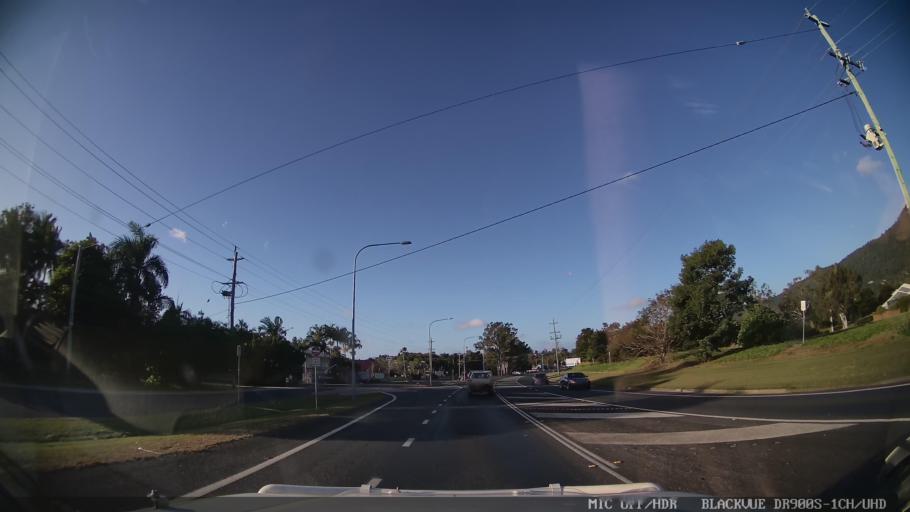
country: AU
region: Queensland
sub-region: Whitsunday
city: Proserpine
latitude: -20.2881
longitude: 148.6782
